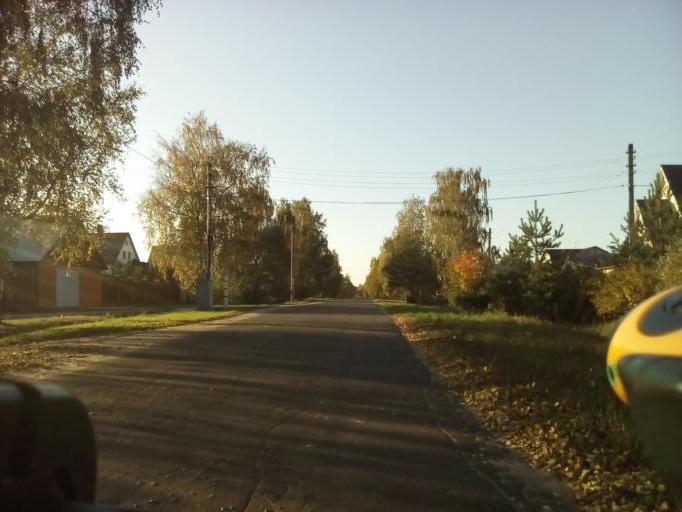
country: RU
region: Moskovskaya
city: Ramenskoye
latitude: 55.6061
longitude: 38.3052
